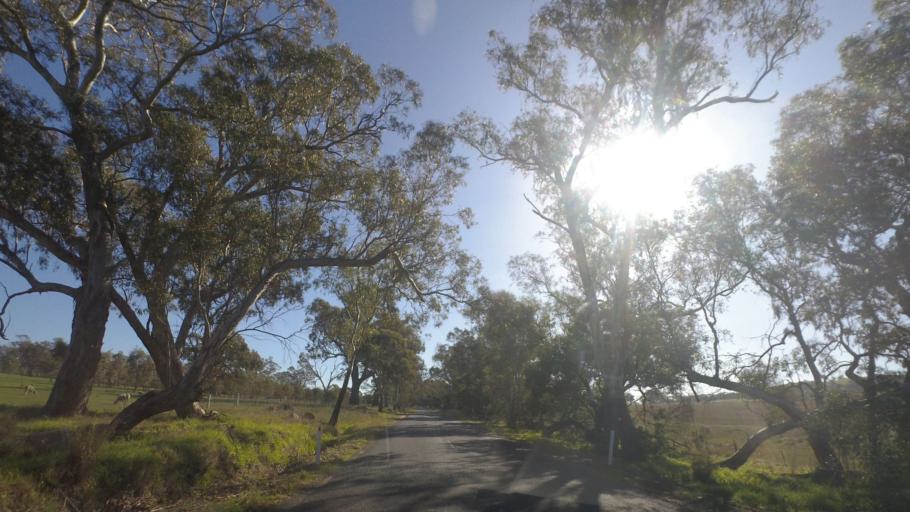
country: AU
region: Victoria
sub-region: Mount Alexander
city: Castlemaine
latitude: -36.9572
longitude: 144.3475
